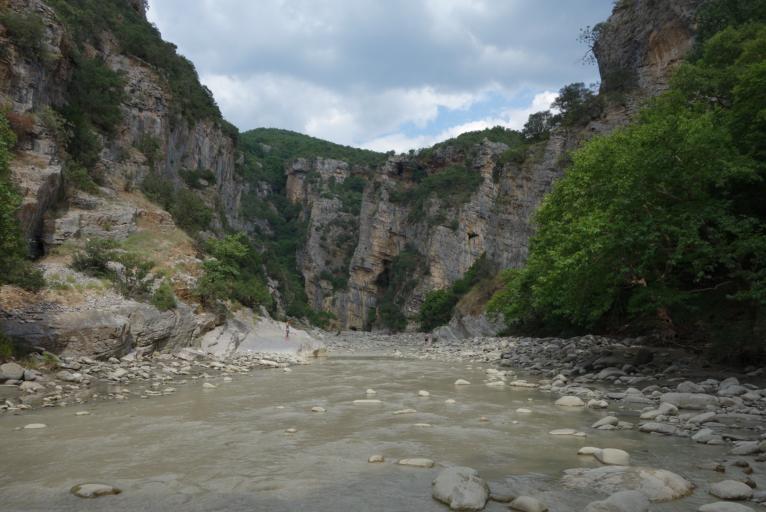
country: AL
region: Gjirokaster
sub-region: Rrethi i Permetit
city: Petran
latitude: 40.2446
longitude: 20.4346
